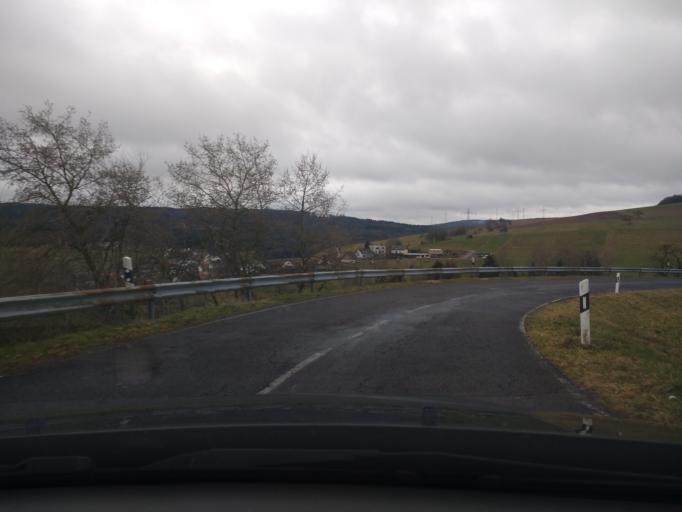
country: DE
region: Rheinland-Pfalz
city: Zerf
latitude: 49.5951
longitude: 6.6717
